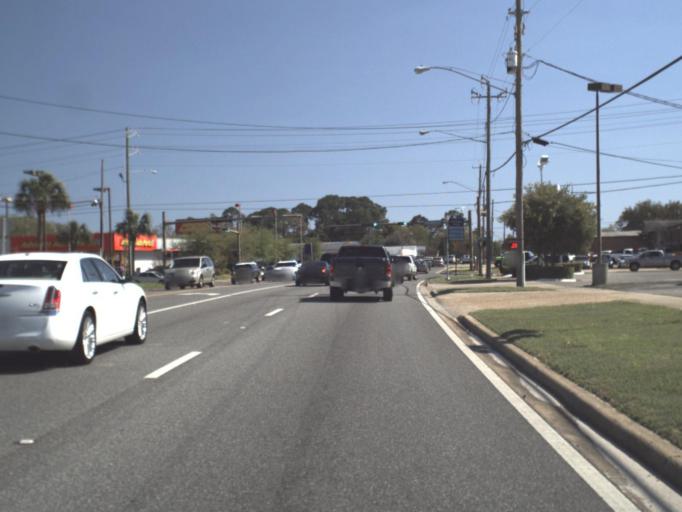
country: US
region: Florida
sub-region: Okaloosa County
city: Fort Walton Beach
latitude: 30.4134
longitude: -86.6132
